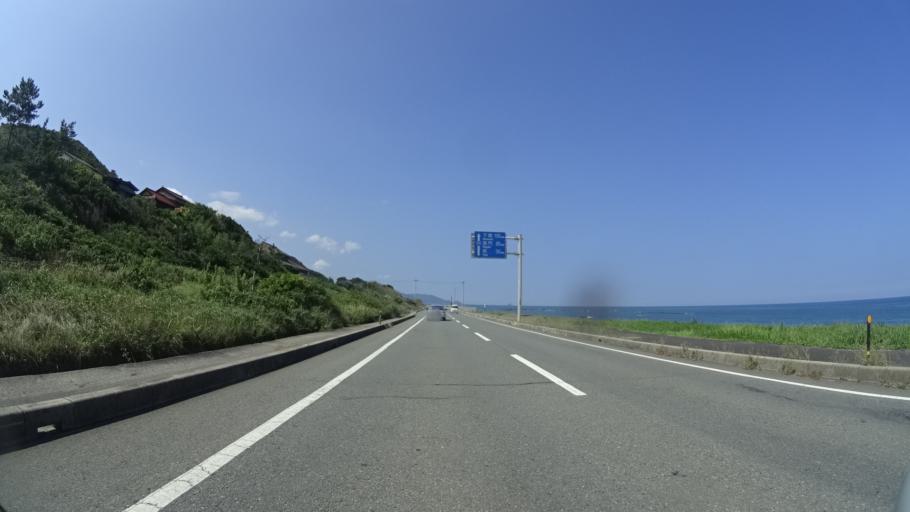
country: JP
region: Shimane
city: Masuda
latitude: 34.6862
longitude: 131.7907
